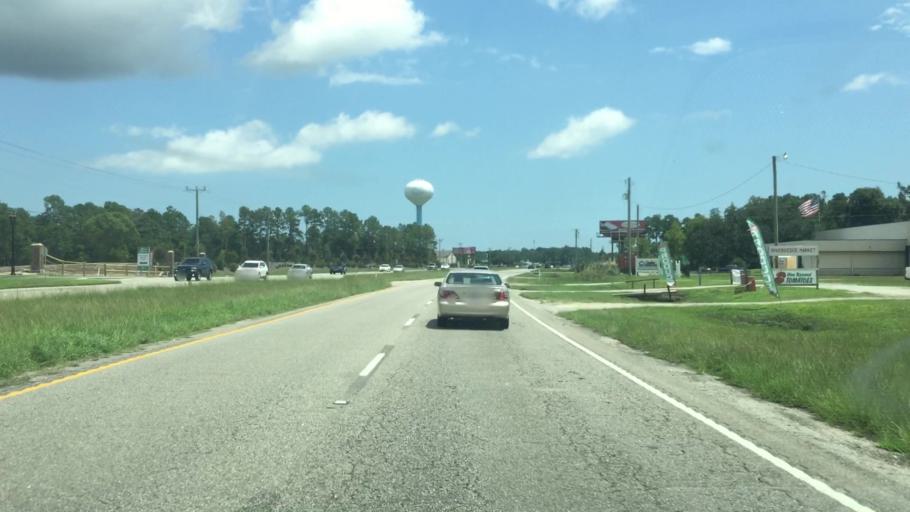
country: US
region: South Carolina
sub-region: Horry County
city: North Myrtle Beach
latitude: 33.9055
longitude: -78.7050
